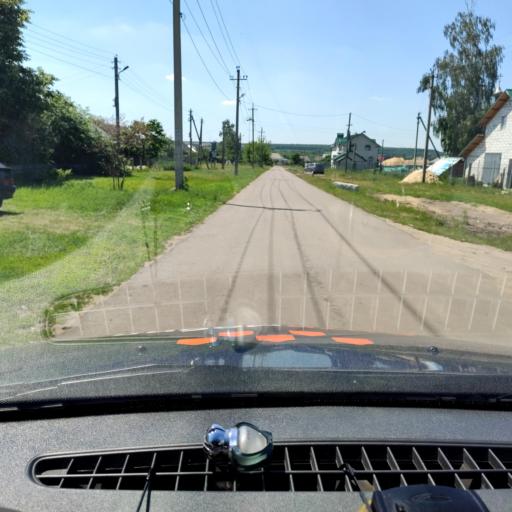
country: RU
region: Voronezj
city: Podgornoye
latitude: 51.8859
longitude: 39.1697
